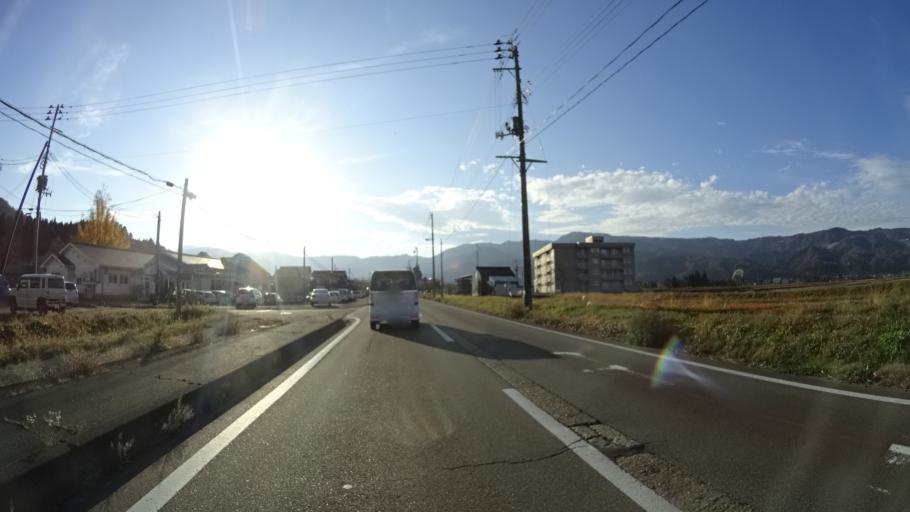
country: JP
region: Niigata
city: Shiozawa
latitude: 37.0070
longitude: 138.8411
